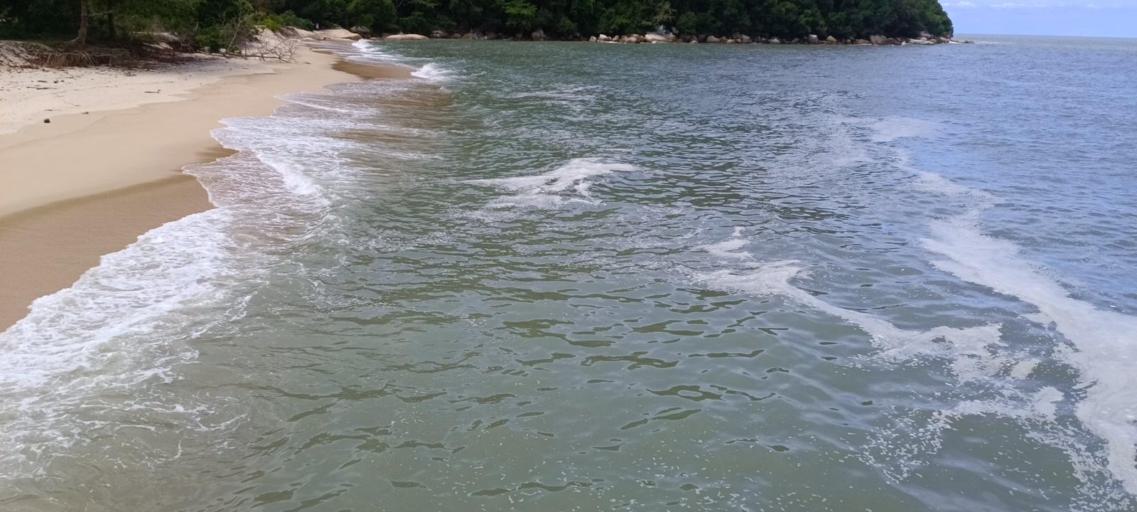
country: MY
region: Penang
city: Tanjung Tokong
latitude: 5.4510
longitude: 100.1826
